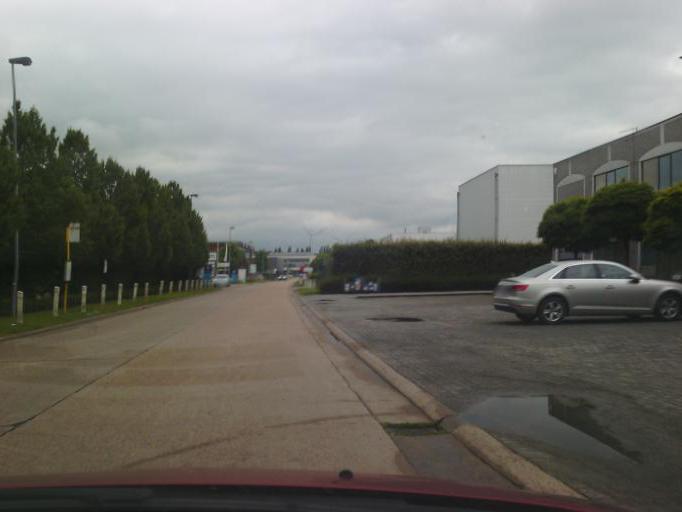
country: BE
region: Flanders
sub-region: Provincie Oost-Vlaanderen
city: Lokeren
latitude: 51.0836
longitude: 4.0098
